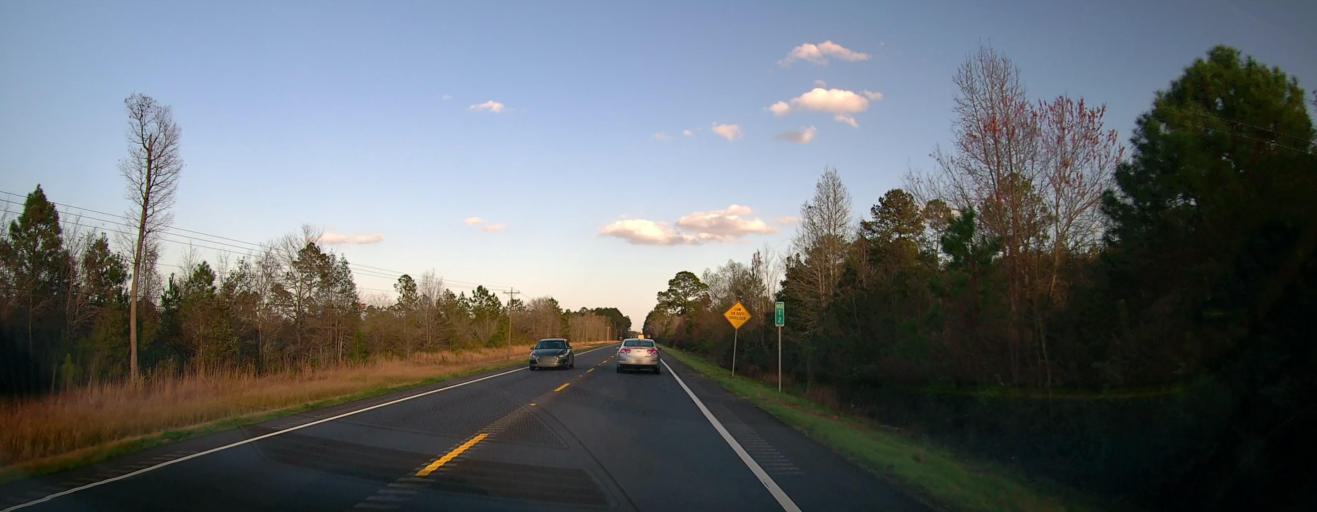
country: US
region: Georgia
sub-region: Bryan County
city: Pembroke
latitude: 32.1326
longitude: -81.5785
